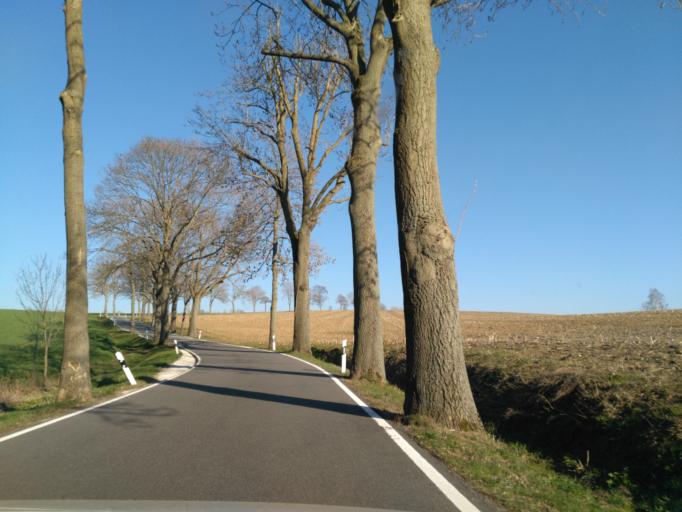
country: DE
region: Saxony
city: Schlettau
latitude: 50.5426
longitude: 12.9732
